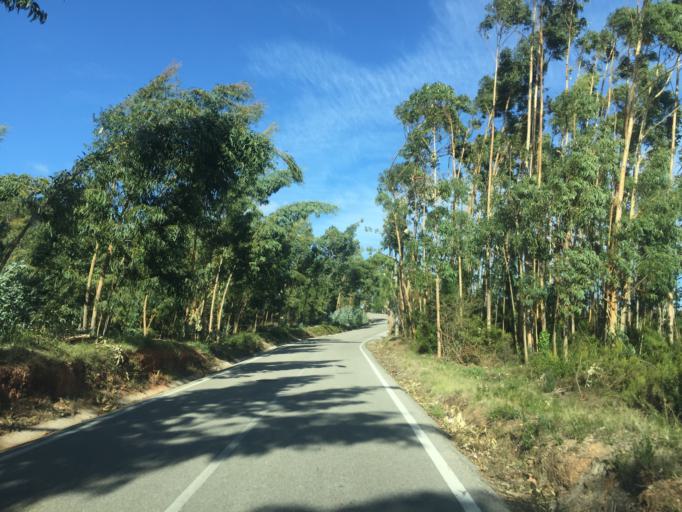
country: PT
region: Coimbra
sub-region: Figueira da Foz
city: Tavarede
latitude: 40.1771
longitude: -8.8380
